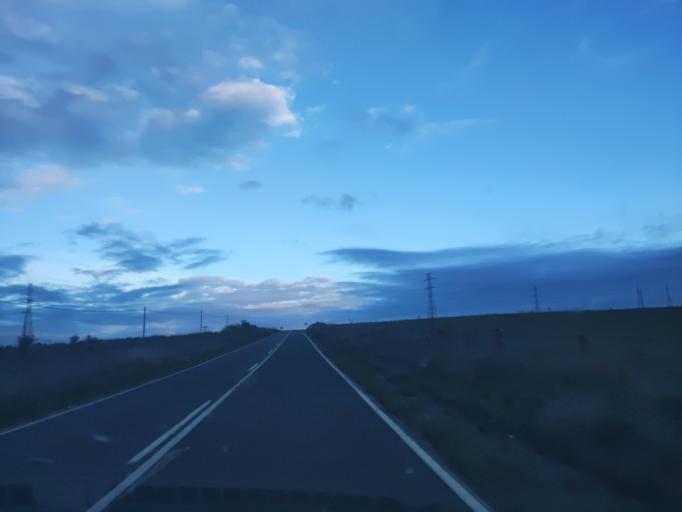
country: ES
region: Castille and Leon
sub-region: Provincia de Salamanca
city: Ciudad Rodrigo
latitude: 40.6241
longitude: -6.5490
